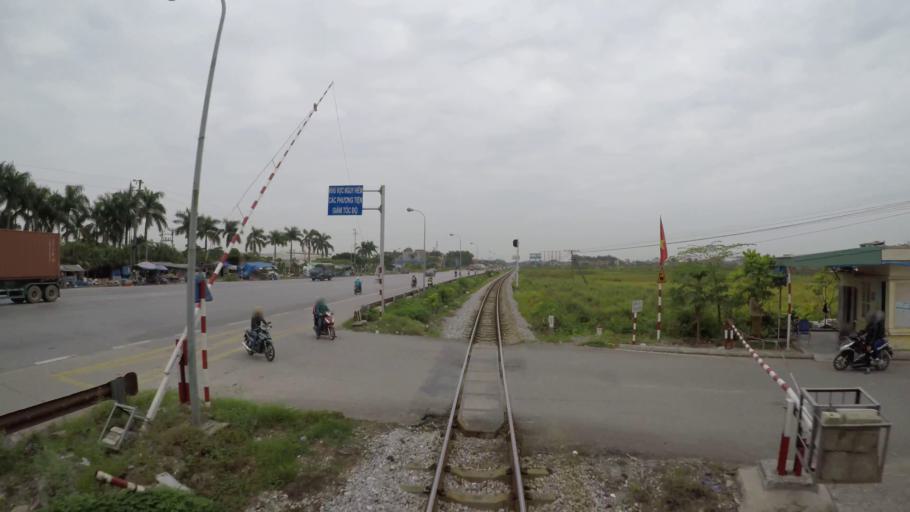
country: VN
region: Hai Duong
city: Phu Thai
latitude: 20.9258
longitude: 106.5570
